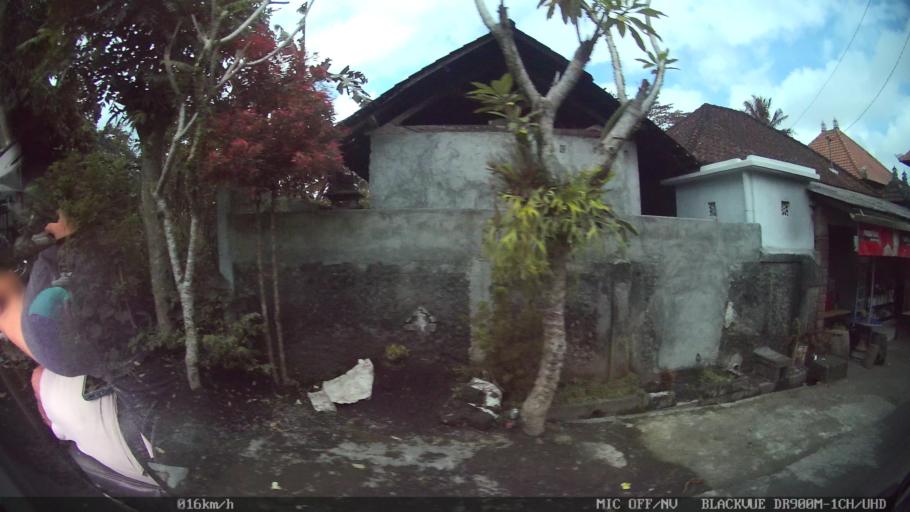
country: ID
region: Bali
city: Banjar Petak
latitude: -8.4475
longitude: 115.3233
